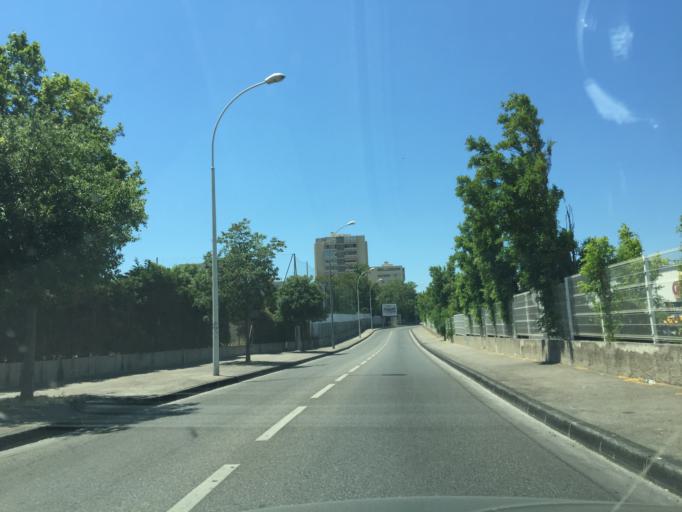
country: FR
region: Provence-Alpes-Cote d'Azur
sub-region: Departement des Bouches-du-Rhone
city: Marseille 09
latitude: 43.2515
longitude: 5.3998
